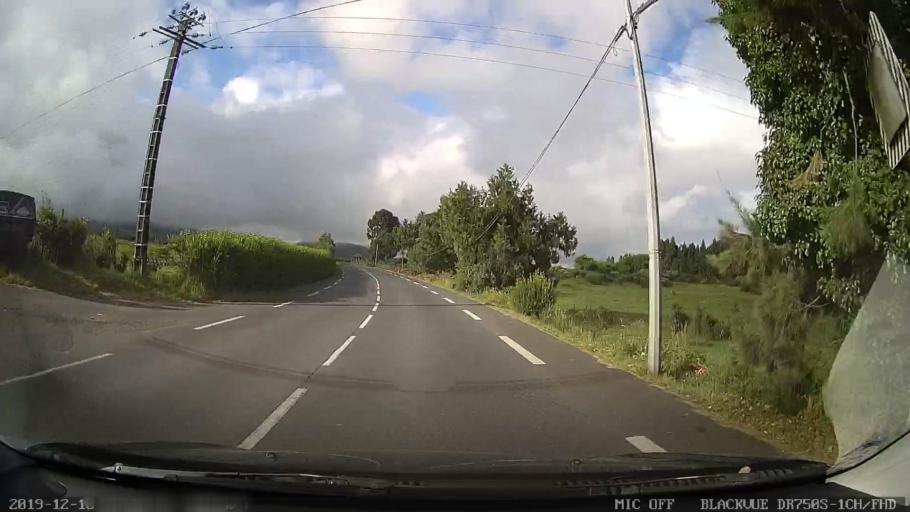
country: RE
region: Reunion
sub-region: Reunion
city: Le Tampon
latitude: -21.1868
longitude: 55.5800
